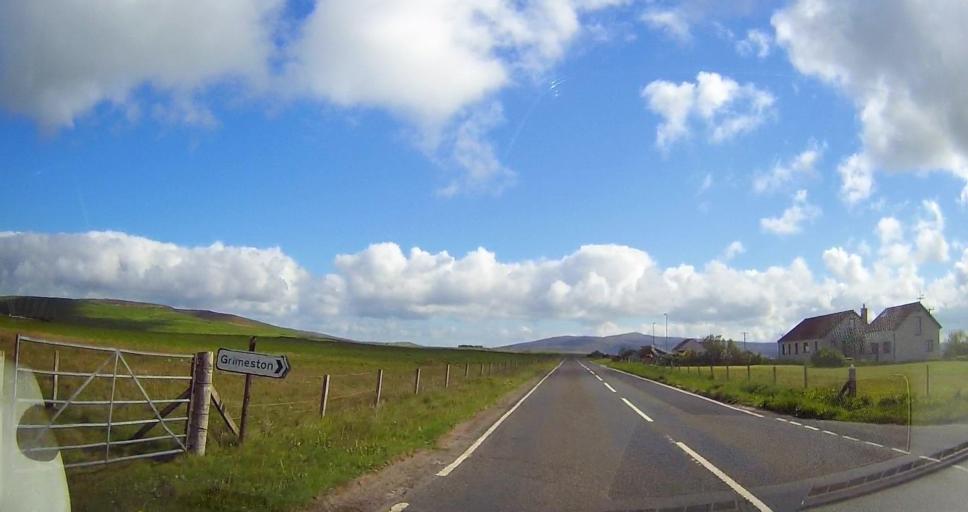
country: GB
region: Scotland
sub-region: Orkney Islands
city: Stromness
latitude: 59.0132
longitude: -3.1559
